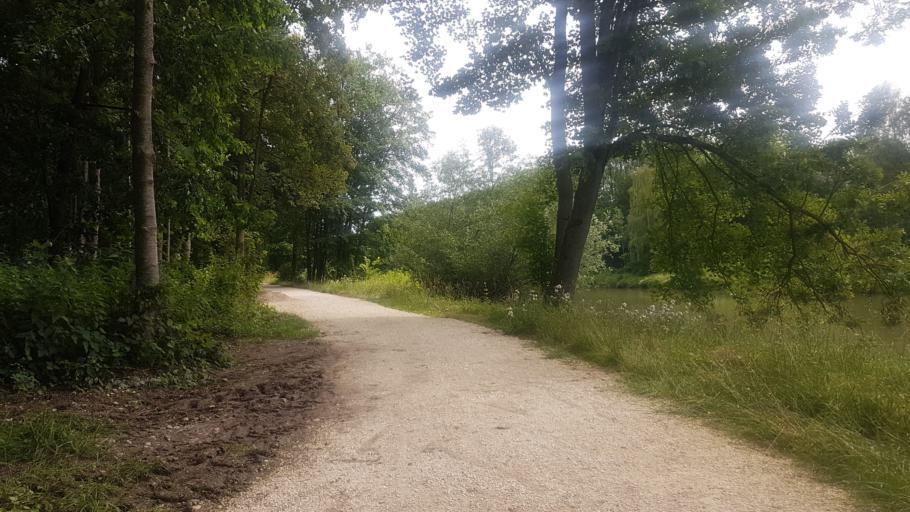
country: DE
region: Bavaria
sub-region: Swabia
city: Lauingen
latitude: 48.5610
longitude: 10.4205
